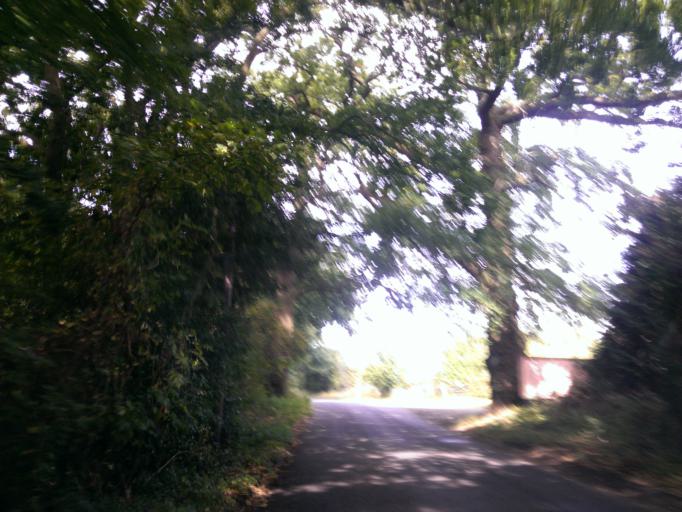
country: GB
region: England
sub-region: Essex
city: Sible Hedingham
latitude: 51.9673
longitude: 0.6238
